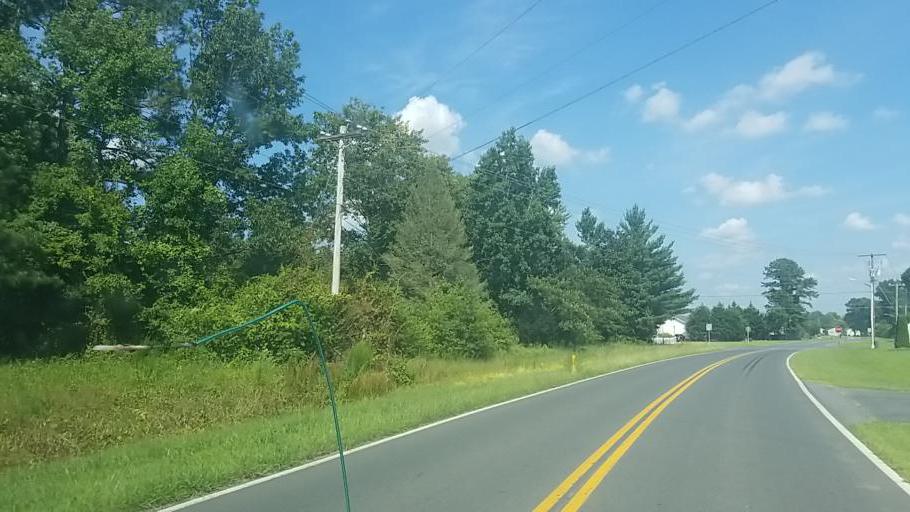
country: US
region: Maryland
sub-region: Wicomico County
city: Fruitland
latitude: 38.3145
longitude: -75.6347
